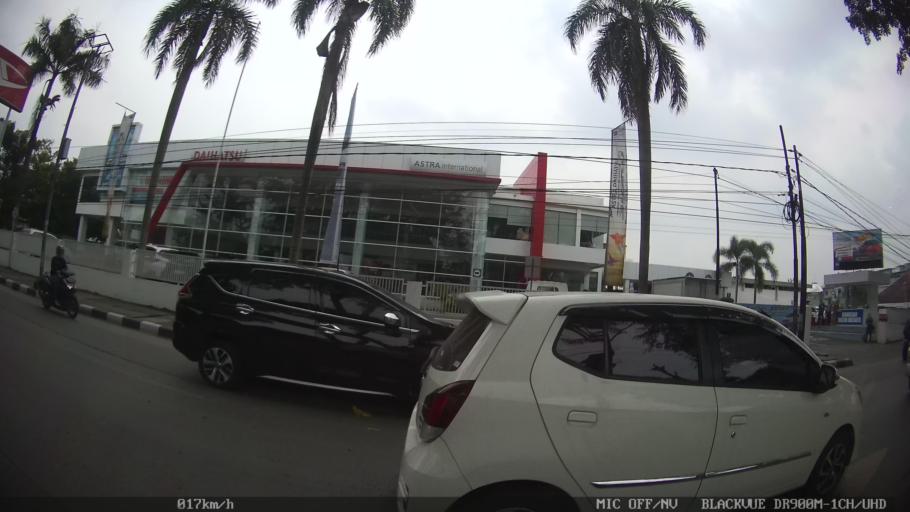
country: ID
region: North Sumatra
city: Medan
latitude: 3.5712
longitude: 98.6895
